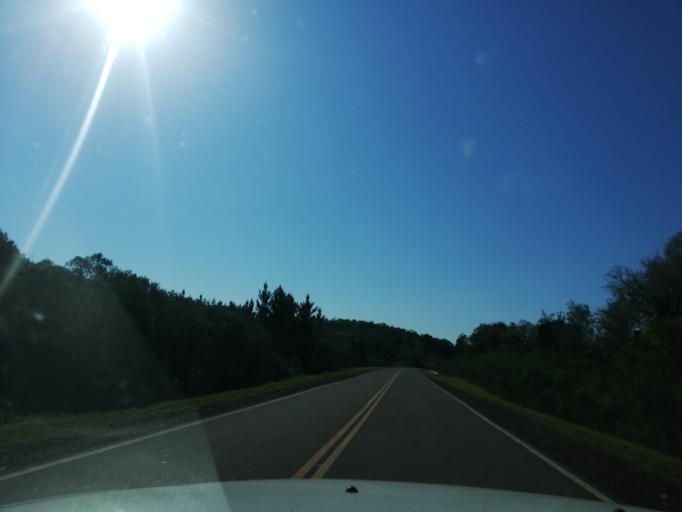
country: AR
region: Misiones
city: Arroyo del Medio
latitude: -27.6840
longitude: -55.3976
